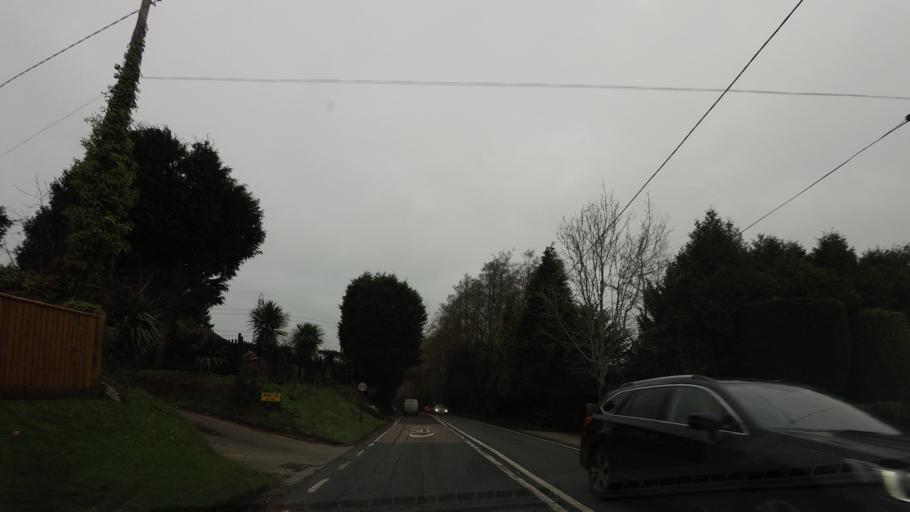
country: GB
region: England
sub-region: East Sussex
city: Saint Leonards-on-Sea
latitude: 50.9119
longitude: 0.5440
